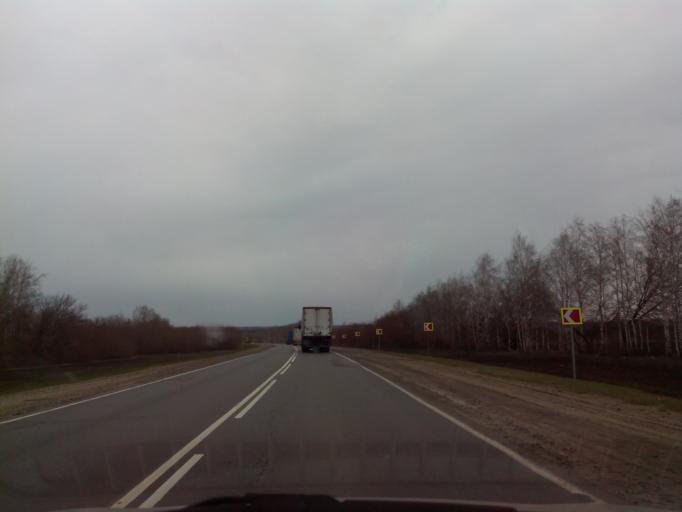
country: RU
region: Tambov
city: Pokrovo-Prigorodnoye
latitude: 52.6707
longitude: 41.3360
